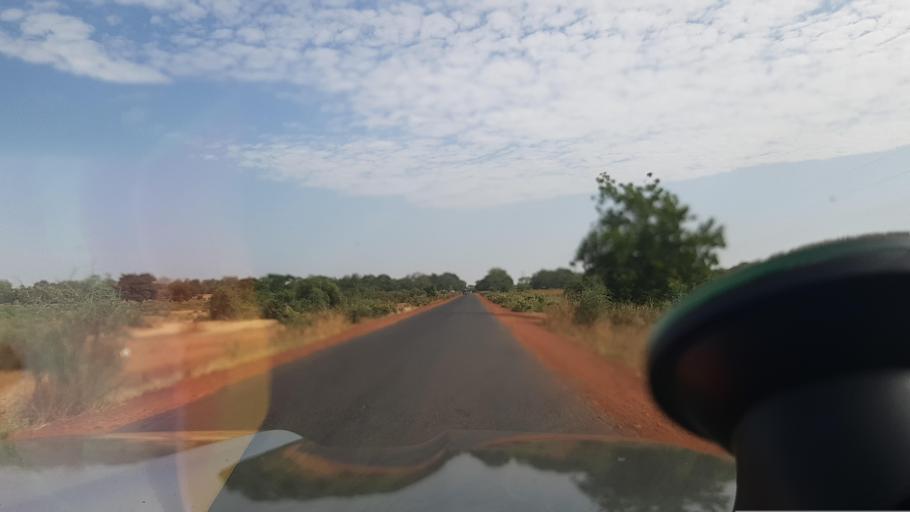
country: ML
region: Segou
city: Segou
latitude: 13.5243
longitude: -6.1321
